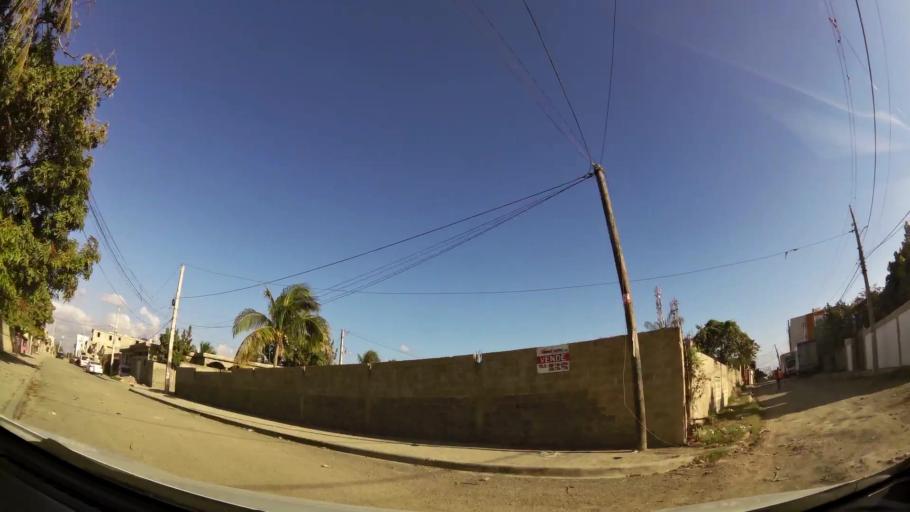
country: DO
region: Santo Domingo
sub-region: Santo Domingo
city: Santo Domingo Este
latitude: 18.4787
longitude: -69.8233
